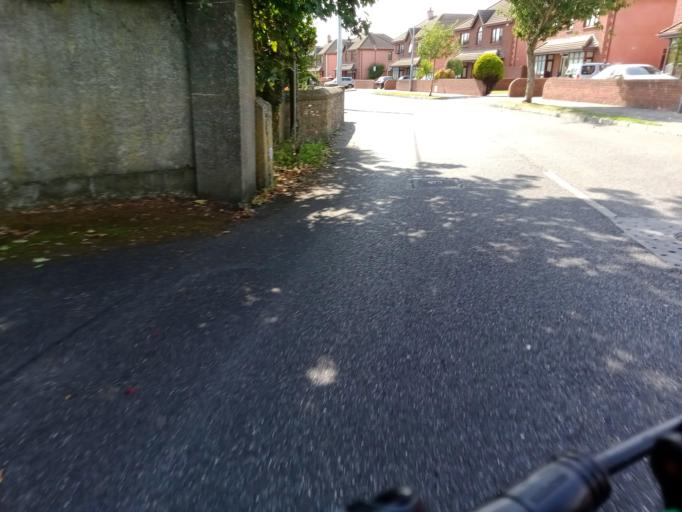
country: IE
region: Munster
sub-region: Waterford
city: Dungarvan
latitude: 52.0913
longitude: -7.6078
